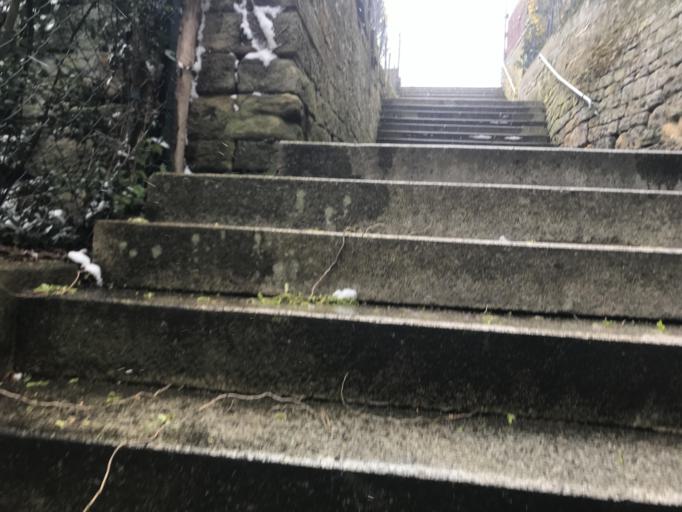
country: DE
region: Rheinland-Pfalz
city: Neustadt
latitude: 49.3484
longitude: 8.1373
